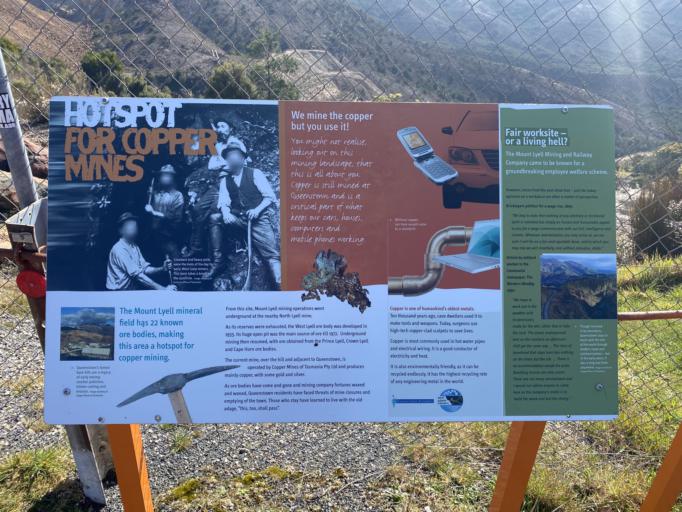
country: AU
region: Tasmania
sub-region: West Coast
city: Queenstown
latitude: -42.0692
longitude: 145.5893
